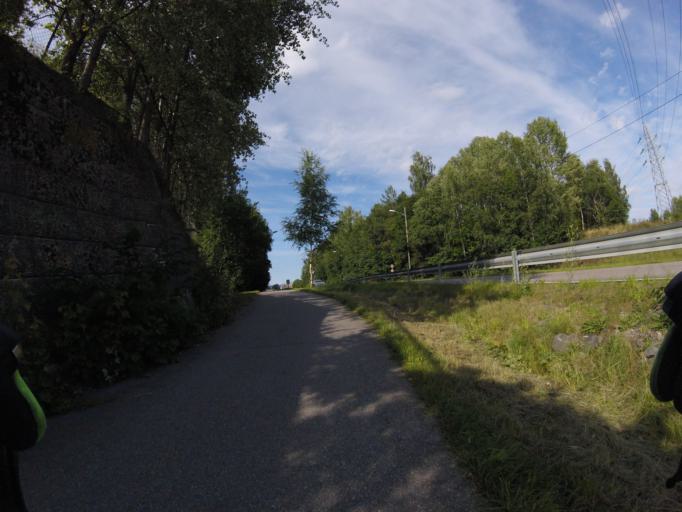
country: NO
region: Akershus
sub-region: Skedsmo
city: Lillestrom
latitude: 59.9741
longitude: 11.0038
